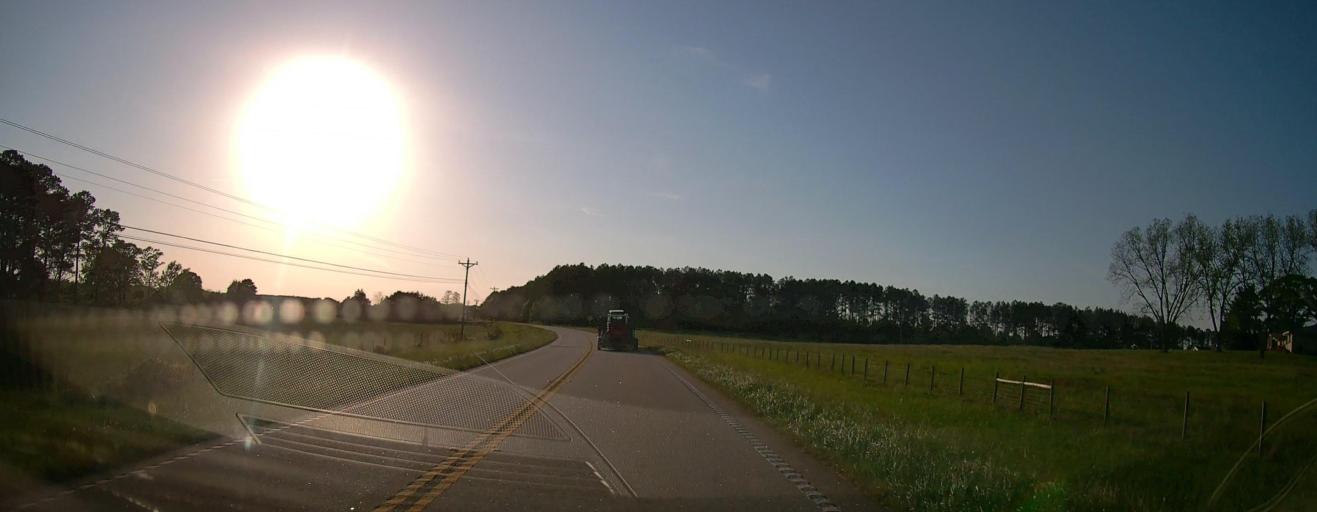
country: US
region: Georgia
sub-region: Walton County
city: Social Circle
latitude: 33.5330
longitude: -83.7128
